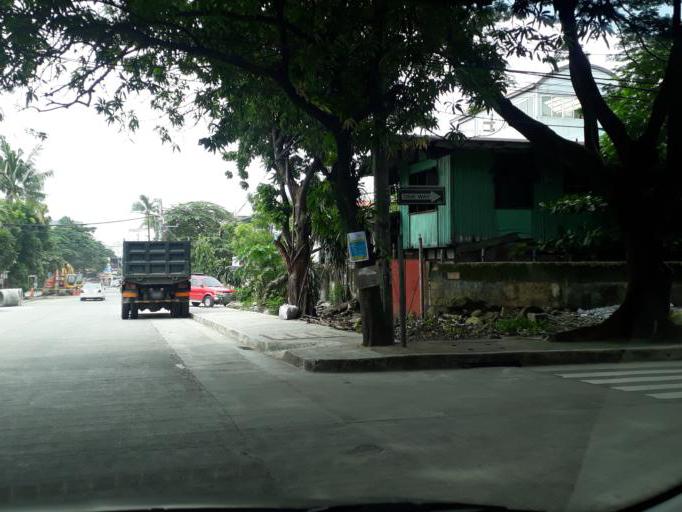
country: PH
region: Metro Manila
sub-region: Quezon City
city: Quezon City
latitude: 14.6315
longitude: 121.0412
